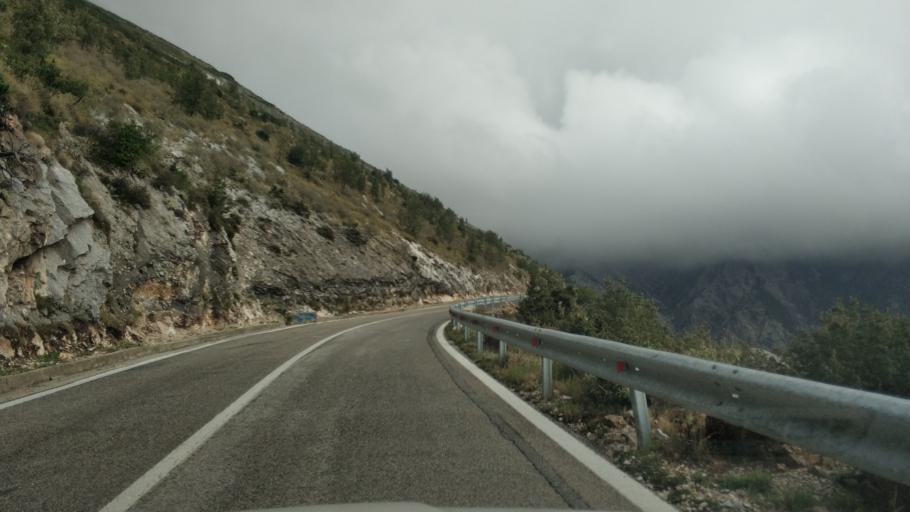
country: AL
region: Vlore
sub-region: Rrethi i Vlores
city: Vranisht
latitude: 40.1891
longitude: 19.6052
